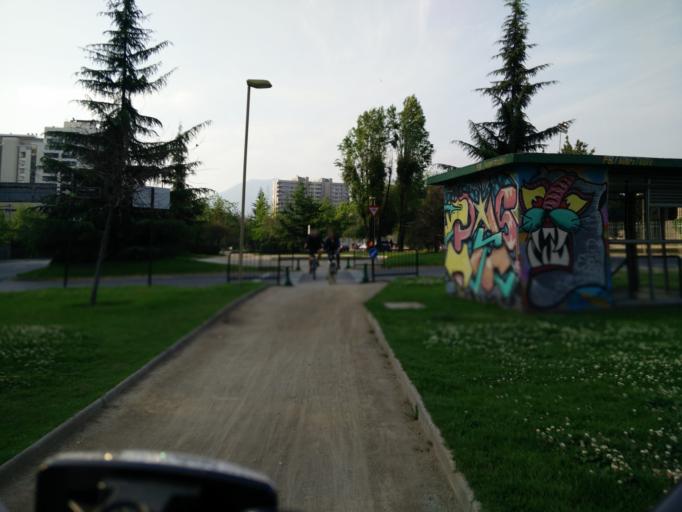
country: CL
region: Santiago Metropolitan
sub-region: Provincia de Santiago
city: Villa Presidente Frei, Nunoa, Santiago, Chile
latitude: -33.4127
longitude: -70.5855
